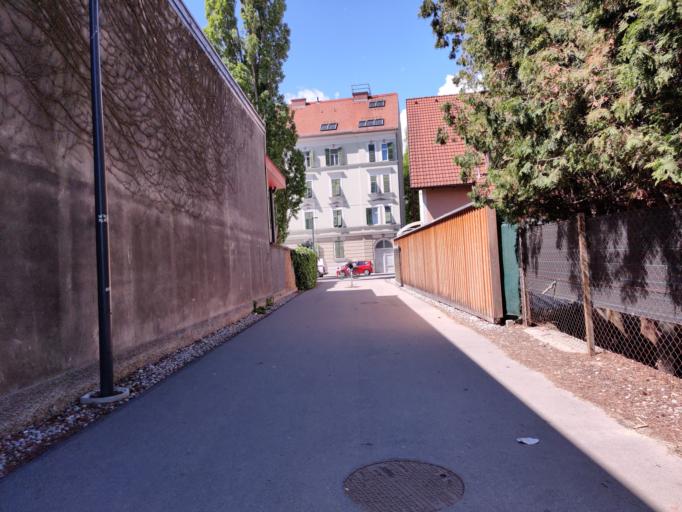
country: AT
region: Styria
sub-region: Graz Stadt
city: Wetzelsdorf
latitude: 47.0752
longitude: 15.4082
